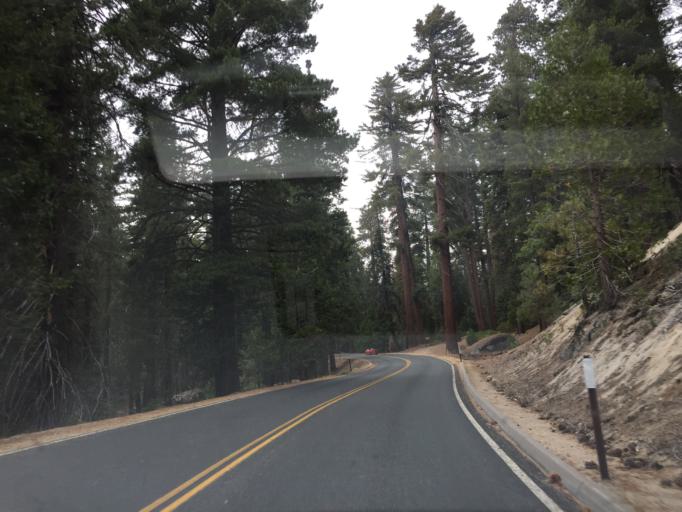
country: US
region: California
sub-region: Fresno County
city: Squaw Valley
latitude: 36.7335
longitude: -118.9628
